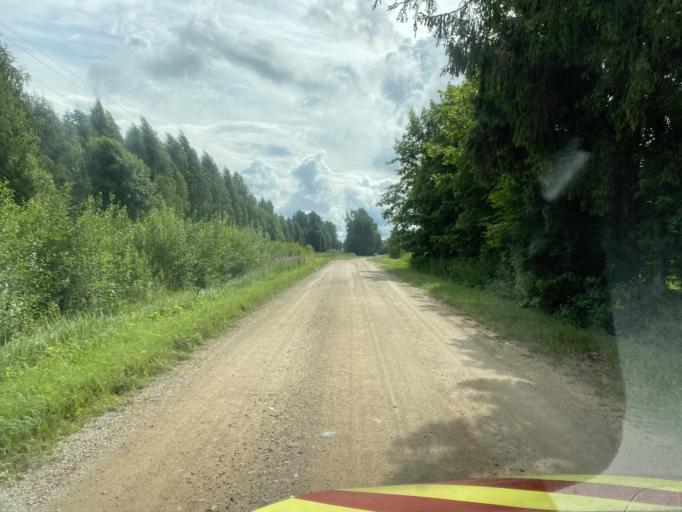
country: EE
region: Viljandimaa
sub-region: Karksi vald
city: Karksi-Nuia
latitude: 58.0862
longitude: 25.4986
